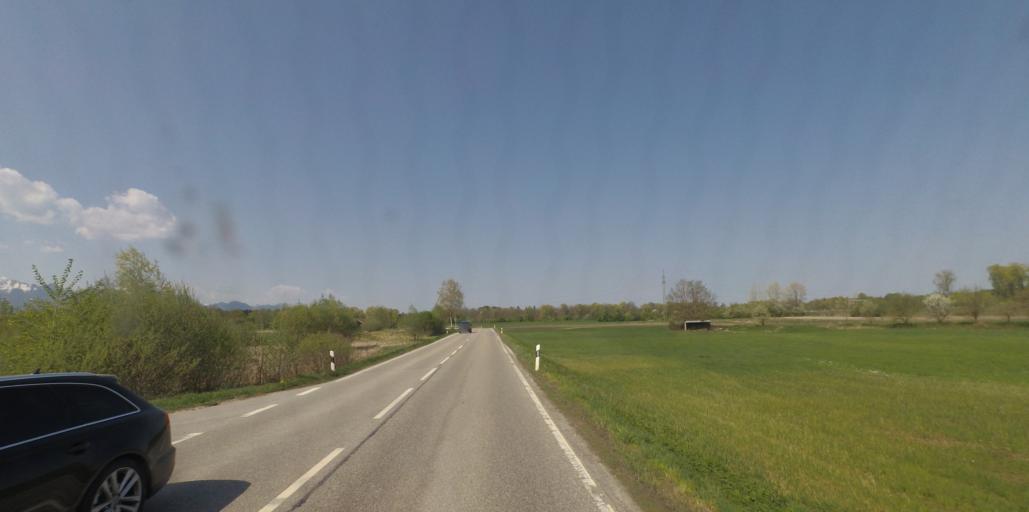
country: DE
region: Bavaria
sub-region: Upper Bavaria
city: Grabenstatt
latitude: 47.8289
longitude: 12.5203
